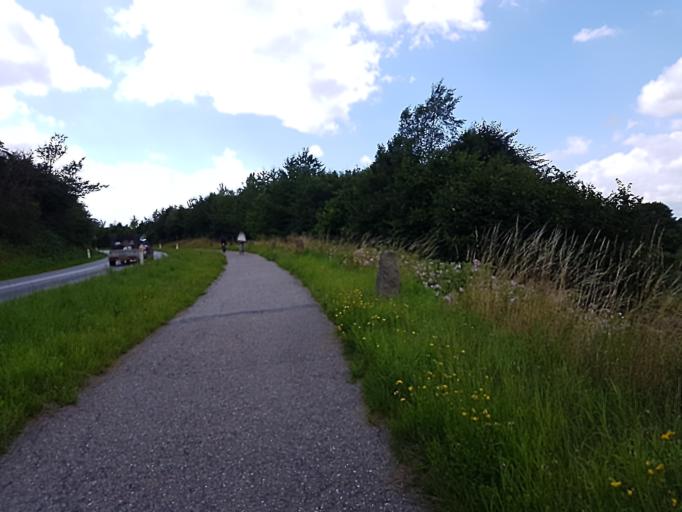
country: DK
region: Capital Region
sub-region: Ballerup Kommune
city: Malov
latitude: 55.7891
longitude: 12.3066
